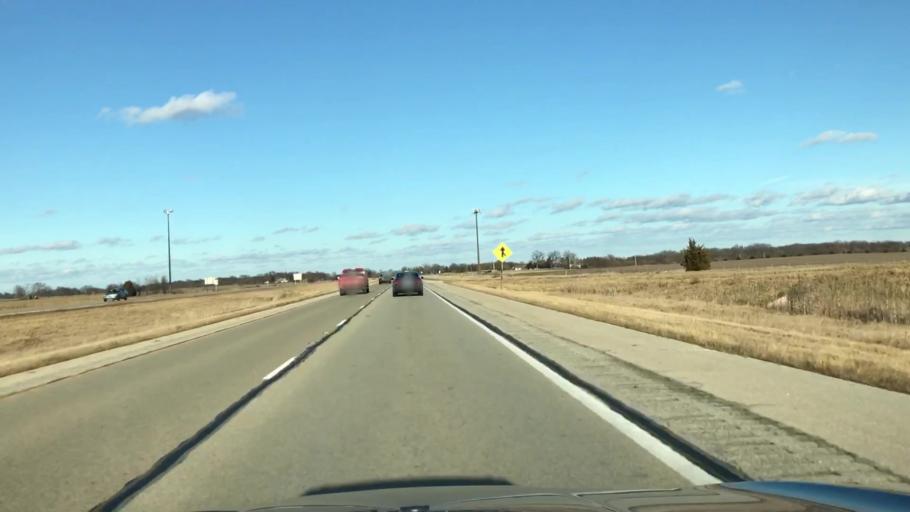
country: US
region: Illinois
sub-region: McLean County
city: Hudson
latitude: 40.5730
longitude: -88.8994
